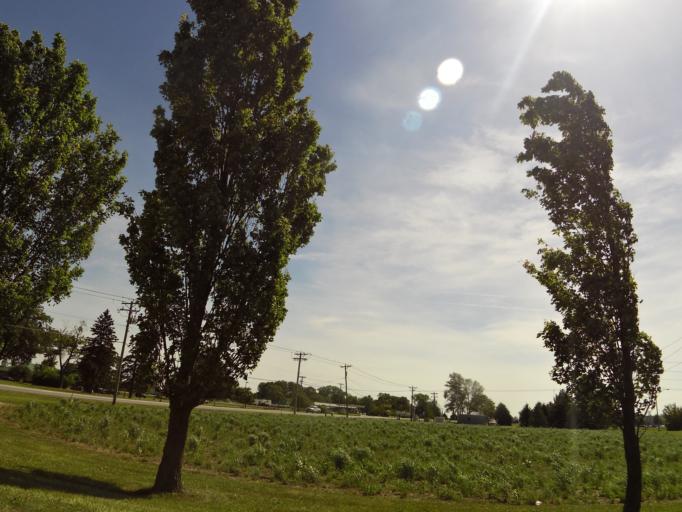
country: US
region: Illinois
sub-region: Vermilion County
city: Danville
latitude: 40.1327
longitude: -87.5545
